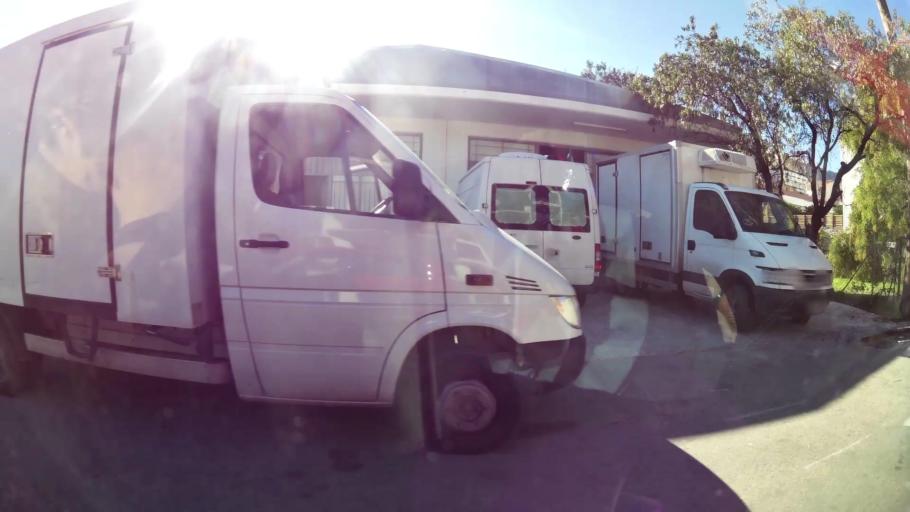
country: GR
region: Attica
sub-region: Nomarchia Anatolikis Attikis
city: Paiania
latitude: 37.9566
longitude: 23.8592
